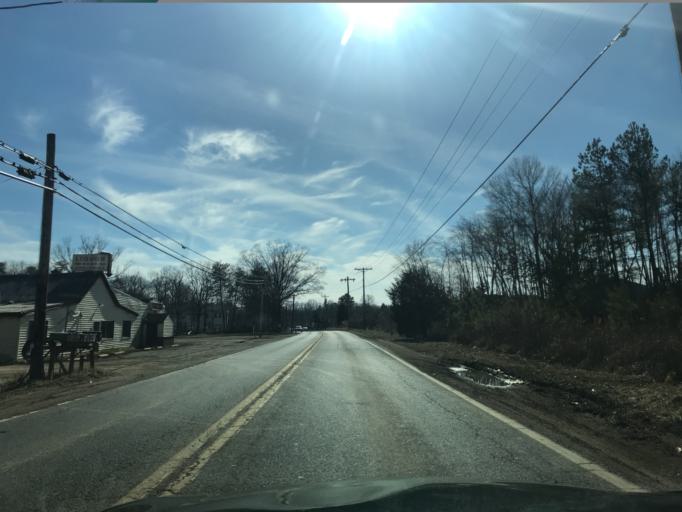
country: US
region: Maryland
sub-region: Charles County
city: Bryans Road
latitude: 38.6188
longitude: -77.0733
